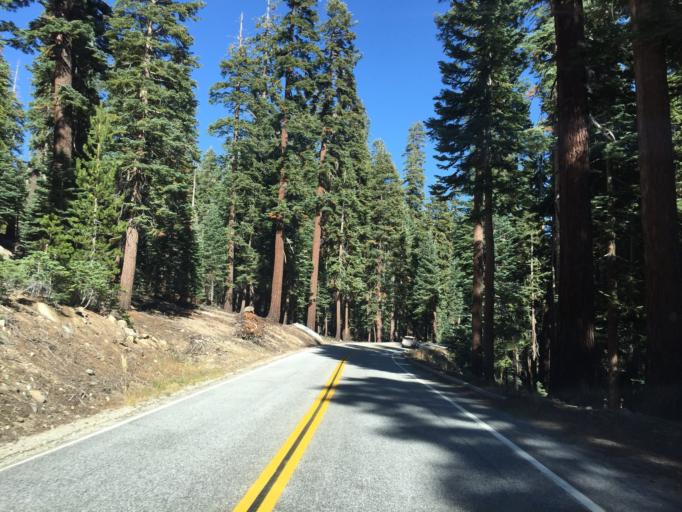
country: US
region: California
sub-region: Mariposa County
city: Yosemite Valley
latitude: 37.8499
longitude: -119.6174
